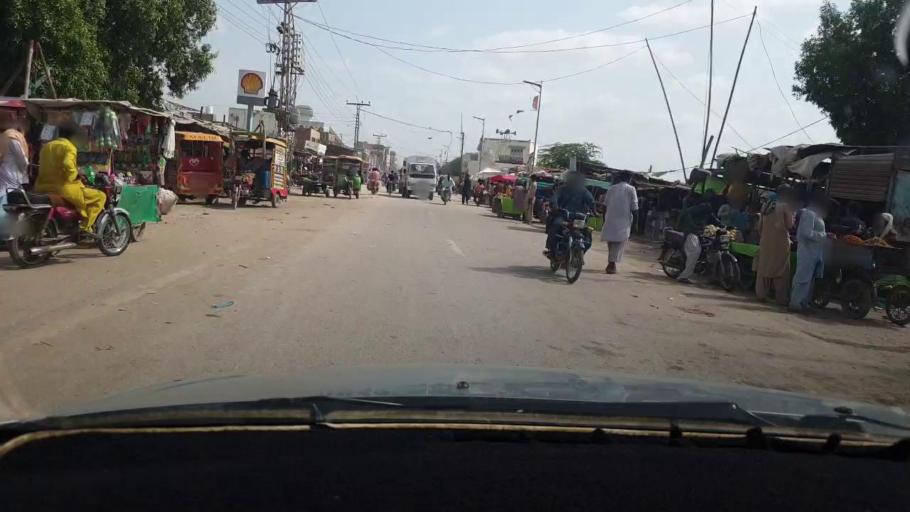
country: PK
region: Sindh
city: Naukot
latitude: 24.9693
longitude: 69.2975
